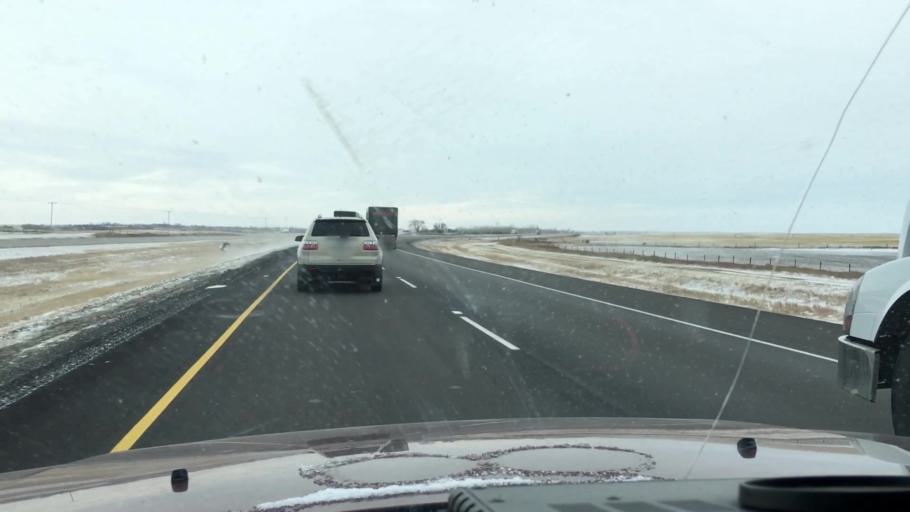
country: CA
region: Saskatchewan
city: Saskatoon
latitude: 51.7815
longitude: -106.4778
